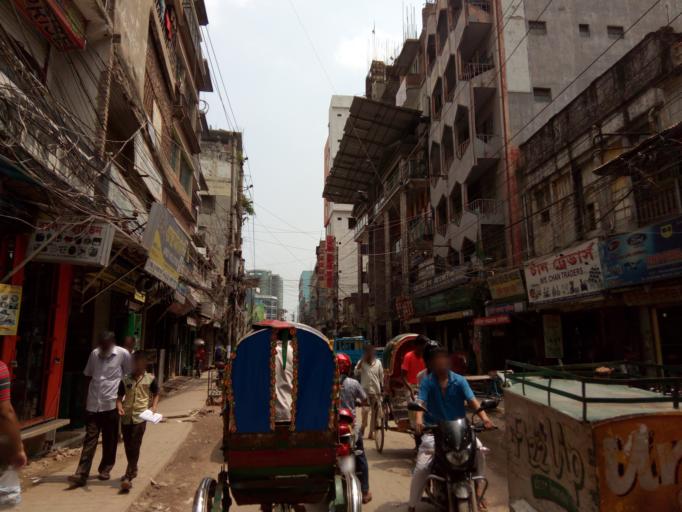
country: BD
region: Dhaka
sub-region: Dhaka
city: Dhaka
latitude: 23.7170
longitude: 90.4114
